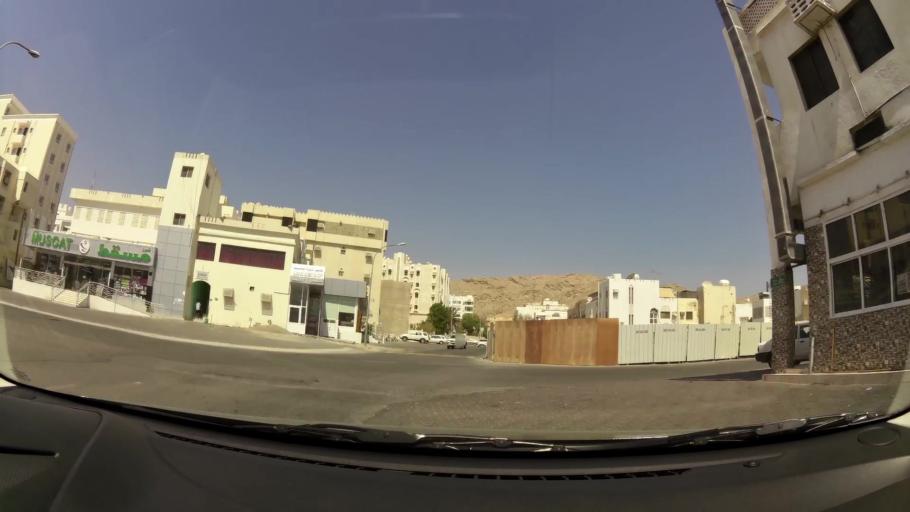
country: OM
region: Muhafazat Masqat
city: Muscat
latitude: 23.6007
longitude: 58.5418
